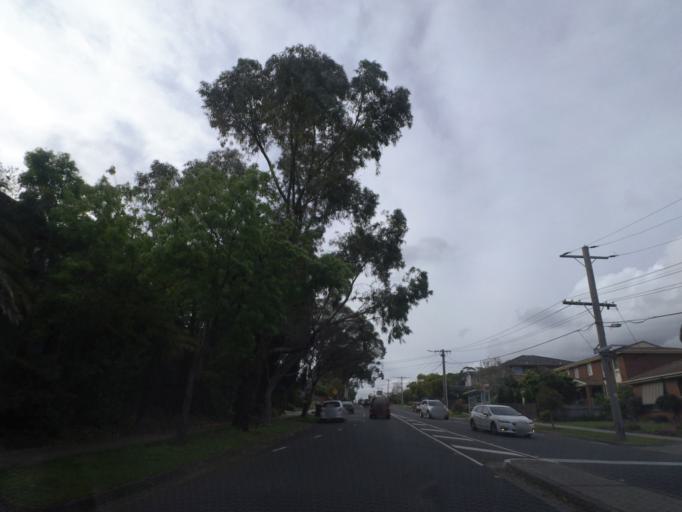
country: AU
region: Victoria
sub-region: Whitehorse
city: Vermont South
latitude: -37.8601
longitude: 145.1823
